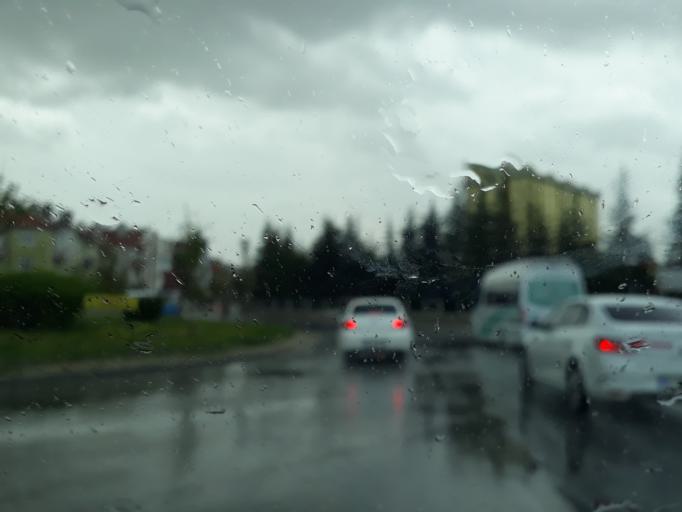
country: TR
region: Konya
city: Selcuklu
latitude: 37.9159
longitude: 32.4924
